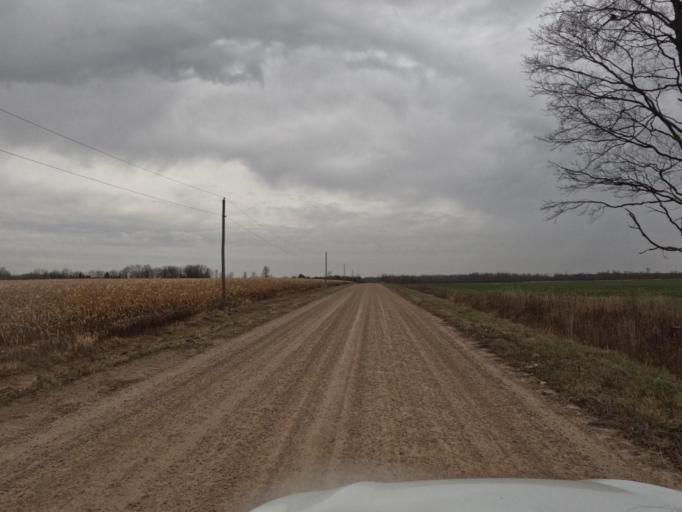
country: CA
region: Ontario
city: Shelburne
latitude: 43.8870
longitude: -80.3824
